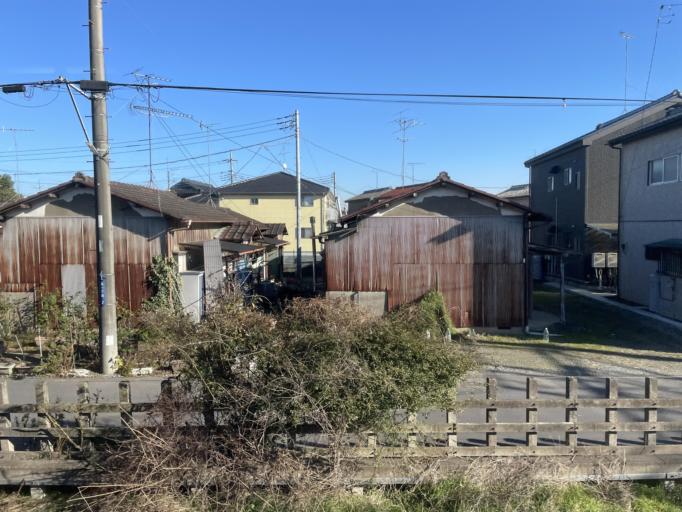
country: JP
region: Saitama
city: Satte
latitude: 36.0845
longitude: 139.7161
